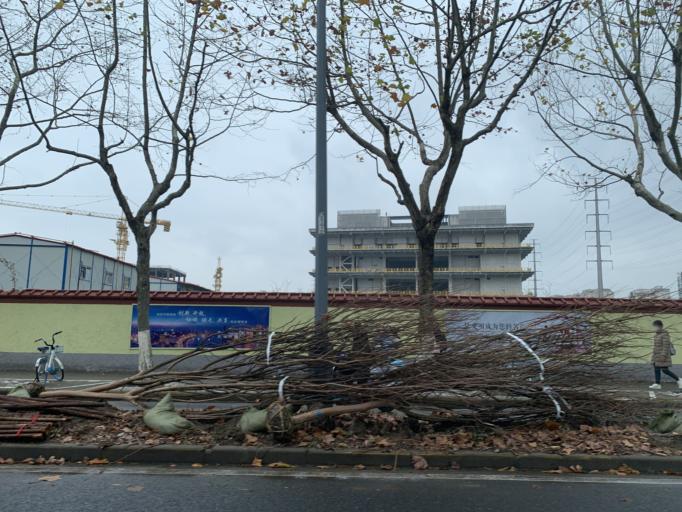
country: CN
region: Shanghai Shi
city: Huamu
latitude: 31.1906
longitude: 121.5359
